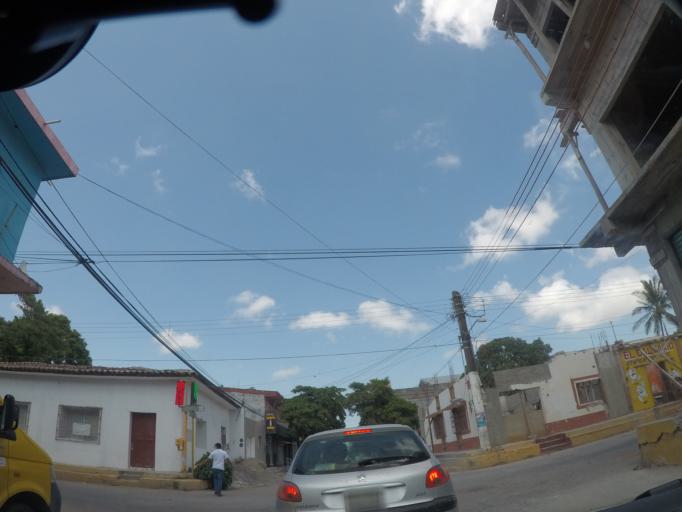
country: MX
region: Oaxaca
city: Juchitan de Zaragoza
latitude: 16.4350
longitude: -95.0200
